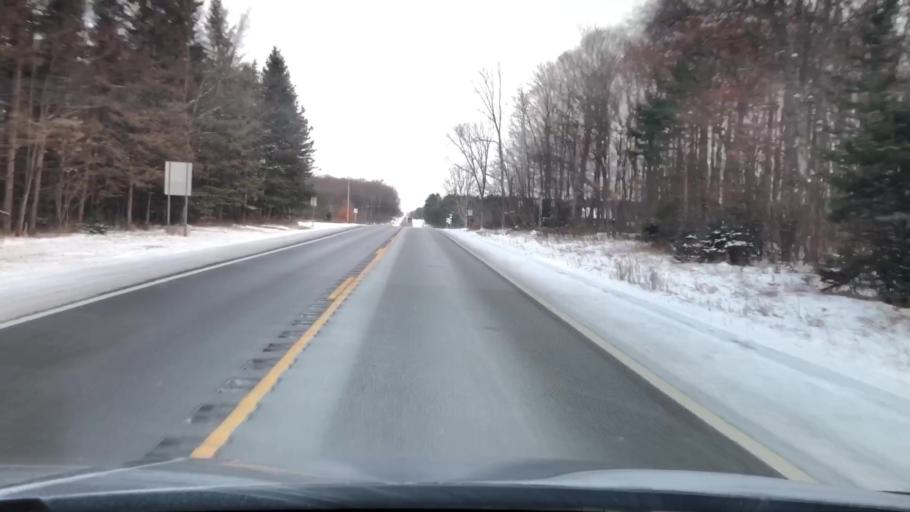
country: US
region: Michigan
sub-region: Grand Traverse County
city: Kingsley
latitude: 44.4672
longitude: -85.6974
